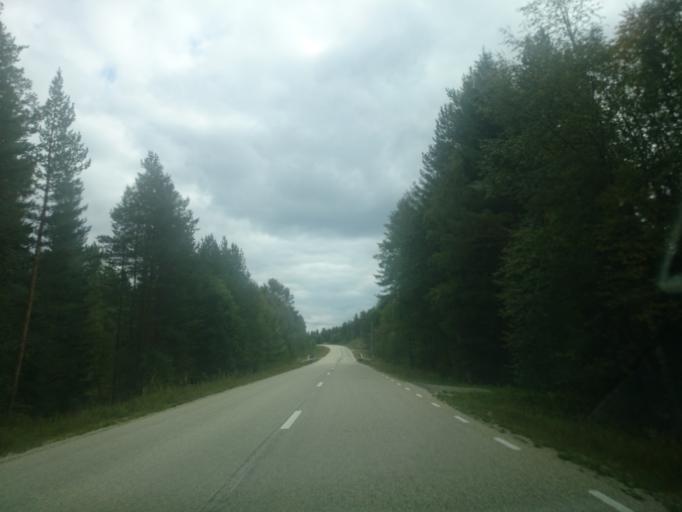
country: SE
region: Jaemtland
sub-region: Harjedalens Kommun
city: Sveg
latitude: 62.4126
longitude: 13.6386
